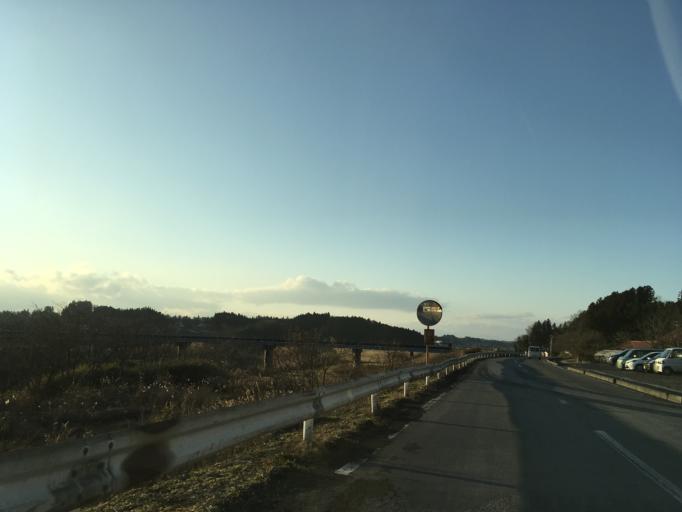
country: JP
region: Iwate
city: Ichinoseki
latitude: 38.8062
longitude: 141.2211
